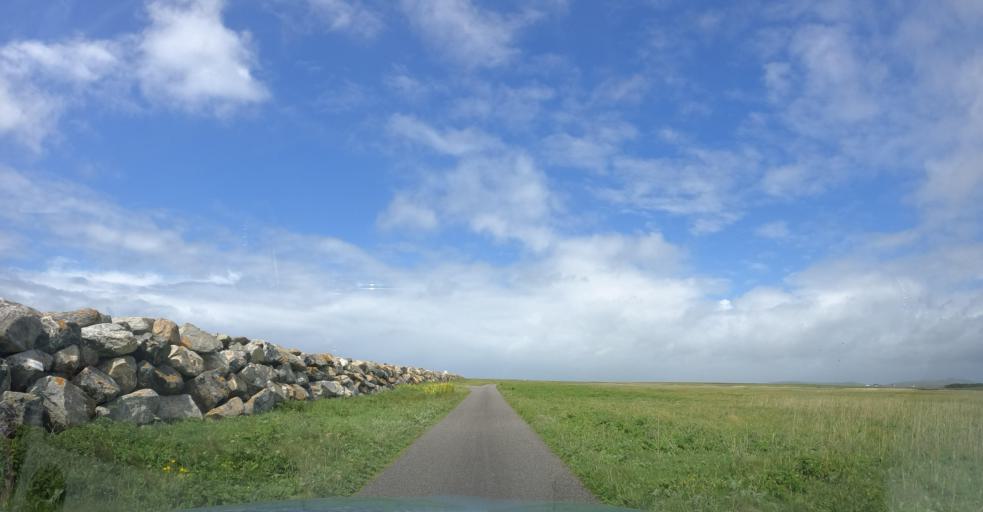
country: GB
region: Scotland
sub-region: Eilean Siar
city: Isle of South Uist
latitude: 57.2817
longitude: -7.4193
